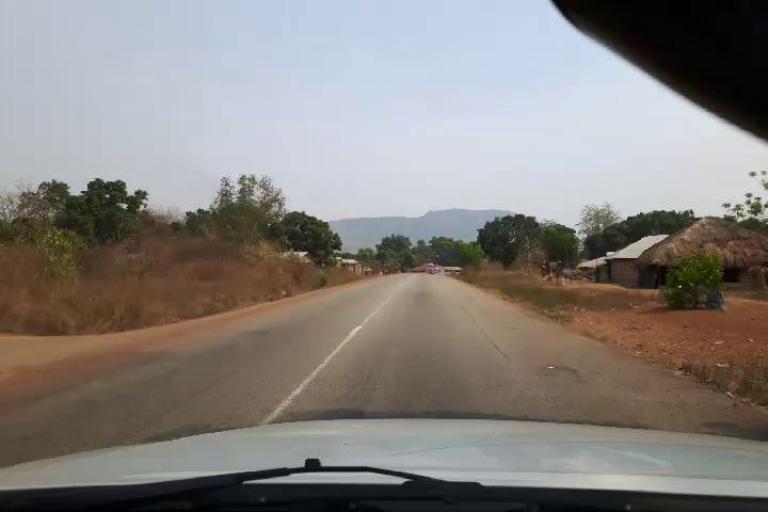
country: SL
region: Northern Province
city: Yonibana
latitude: 8.4009
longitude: -12.1955
